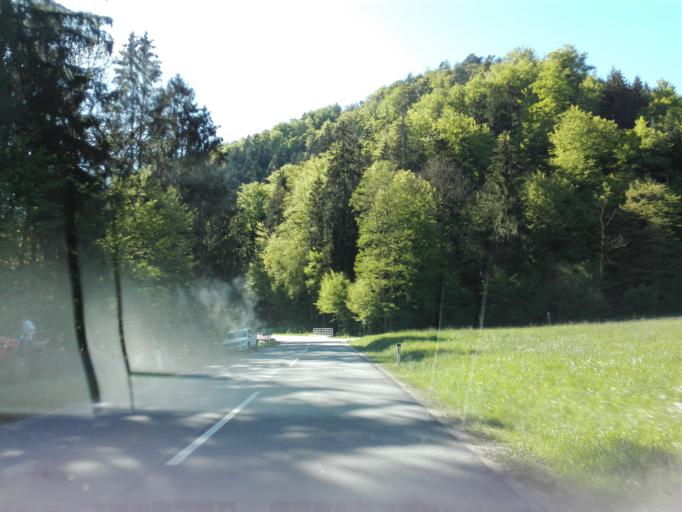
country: AT
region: Upper Austria
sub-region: Politischer Bezirk Perg
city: Perg
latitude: 48.2802
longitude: 14.6449
